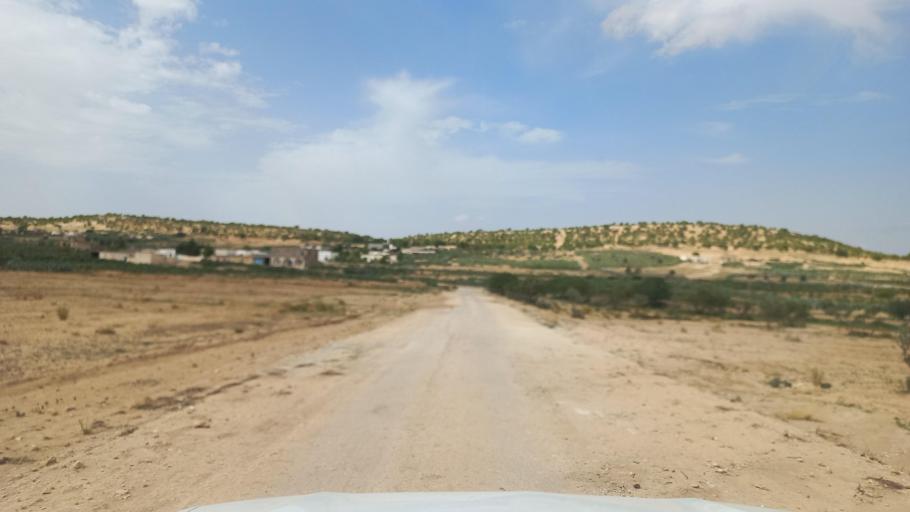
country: TN
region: Al Qasrayn
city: Kasserine
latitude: 35.3869
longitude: 8.8637
